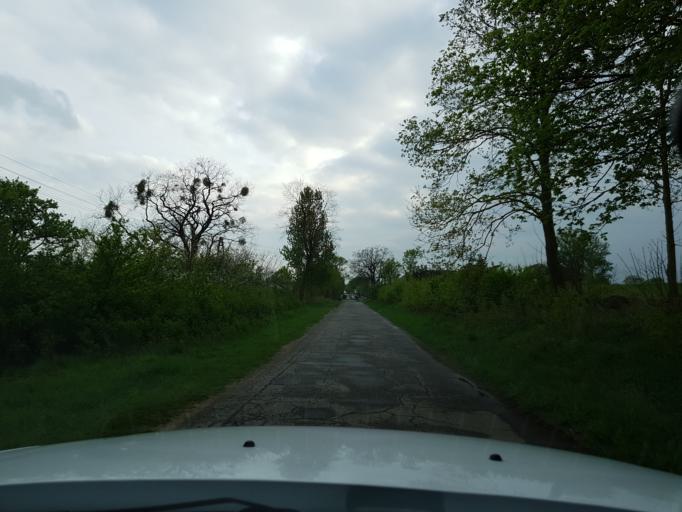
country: PL
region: West Pomeranian Voivodeship
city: Trzcinsko Zdroj
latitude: 52.9787
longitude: 14.6727
